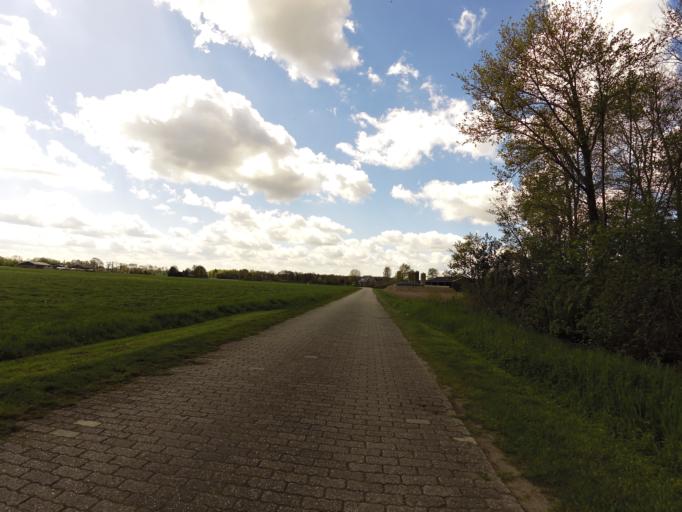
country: NL
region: Gelderland
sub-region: Gemeente Doesburg
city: Doesburg
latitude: 51.9356
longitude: 6.1782
